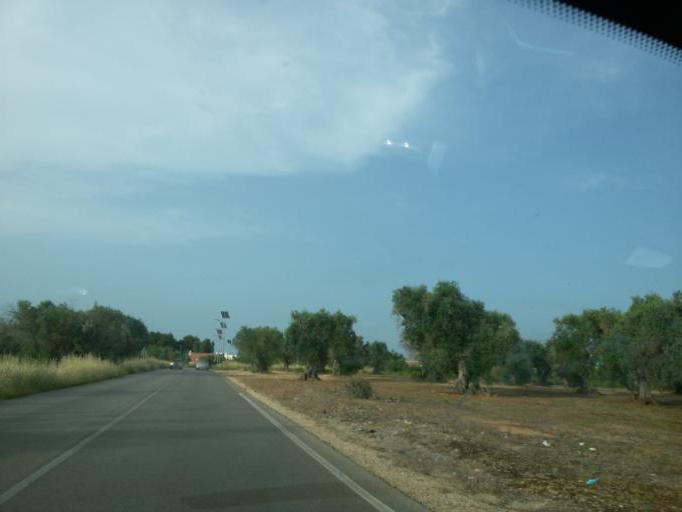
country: IT
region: Apulia
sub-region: Provincia di Brindisi
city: San Pietro Vernotico
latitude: 40.4827
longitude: 17.9859
